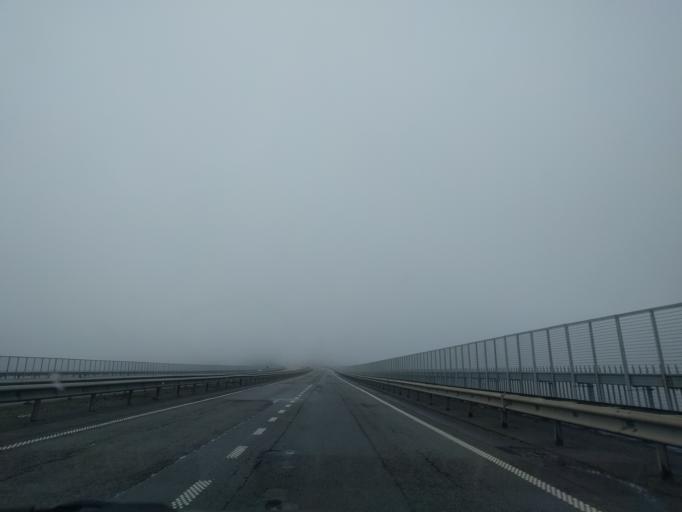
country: BE
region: Wallonia
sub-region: Province de Namur
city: Dinant
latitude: 50.2411
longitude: 4.9198
